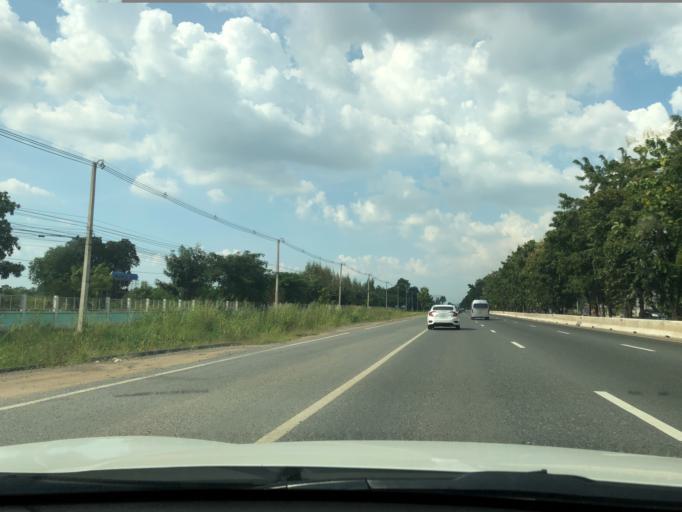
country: TH
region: Nakhon Sawan
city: Krok Phra
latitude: 15.5800
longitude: 100.1245
